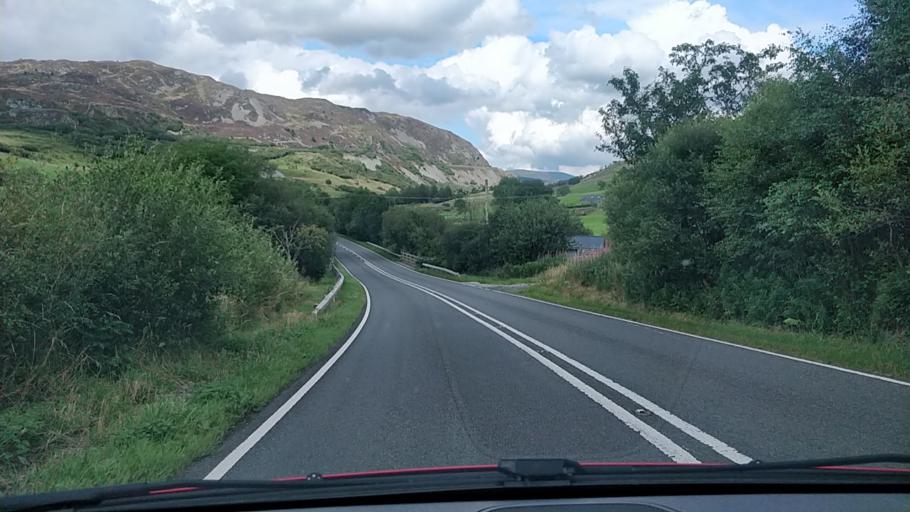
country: GB
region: Wales
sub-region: Gwynedd
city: Trawsfynydd
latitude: 52.9100
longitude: -3.8535
